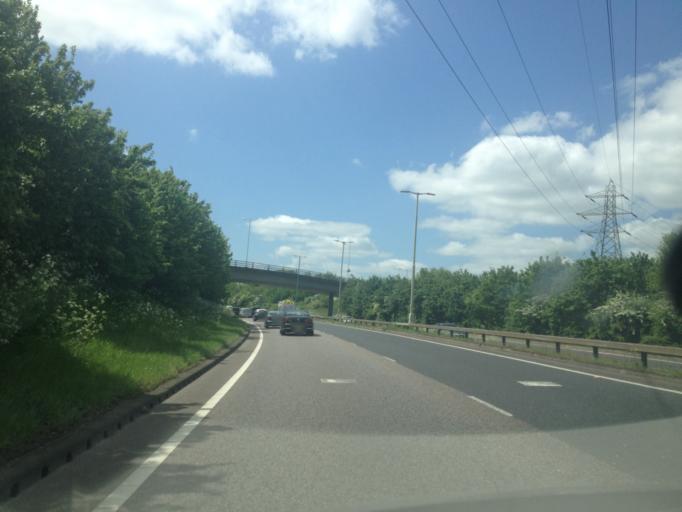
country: GB
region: England
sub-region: Hertfordshire
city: Watford
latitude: 51.6702
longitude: -0.3768
